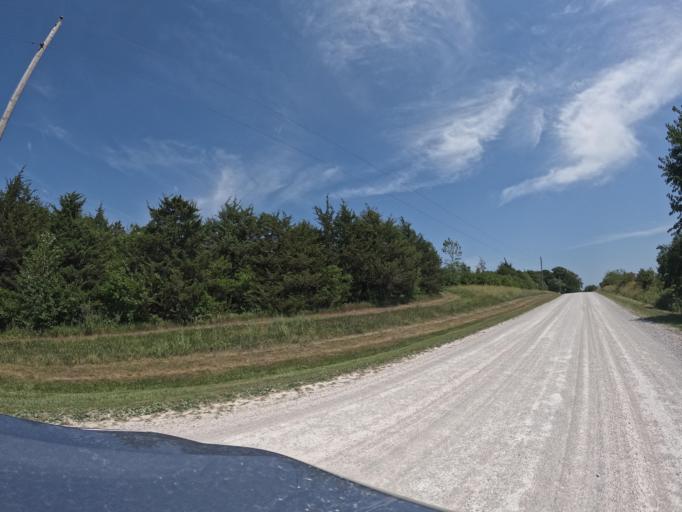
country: US
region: Iowa
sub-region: Henry County
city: Mount Pleasant
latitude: 40.9306
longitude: -91.6208
